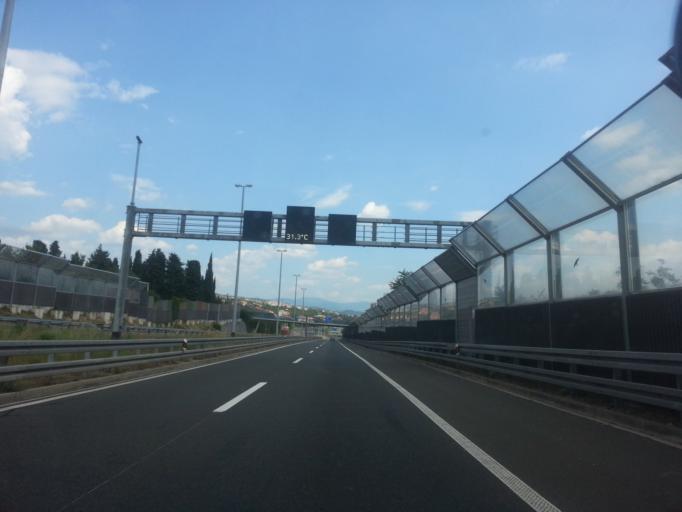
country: HR
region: Primorsko-Goranska
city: Marinici
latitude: 45.3476
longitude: 14.3827
